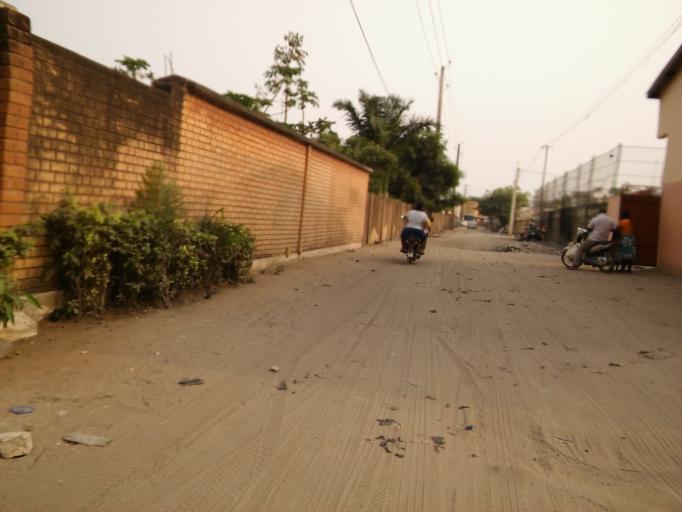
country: BJ
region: Littoral
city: Cotonou
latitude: 6.3583
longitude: 2.4012
